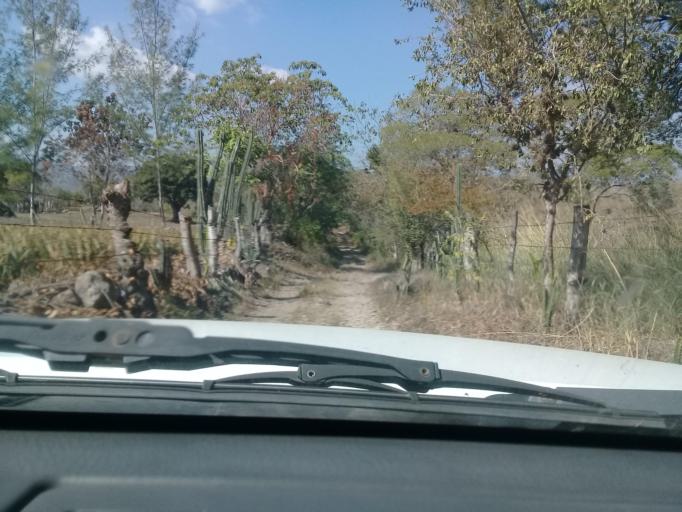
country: MX
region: Veracruz
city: Actopan
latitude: 19.4819
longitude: -96.6482
